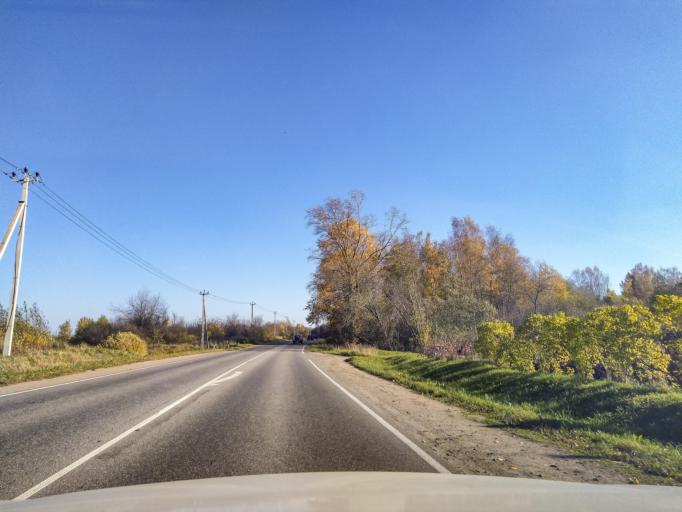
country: RU
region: Leningrad
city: Rozhdestveno
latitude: 59.3465
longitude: 29.9704
